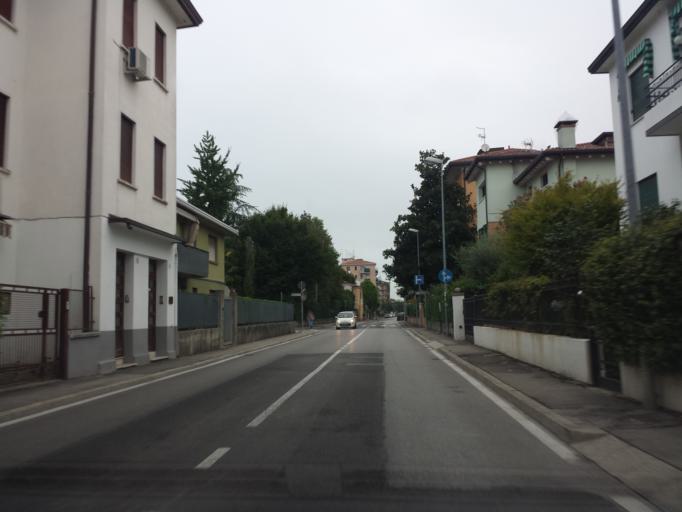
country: IT
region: Veneto
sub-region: Provincia di Padova
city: Padova
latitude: 45.4220
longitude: 11.8780
